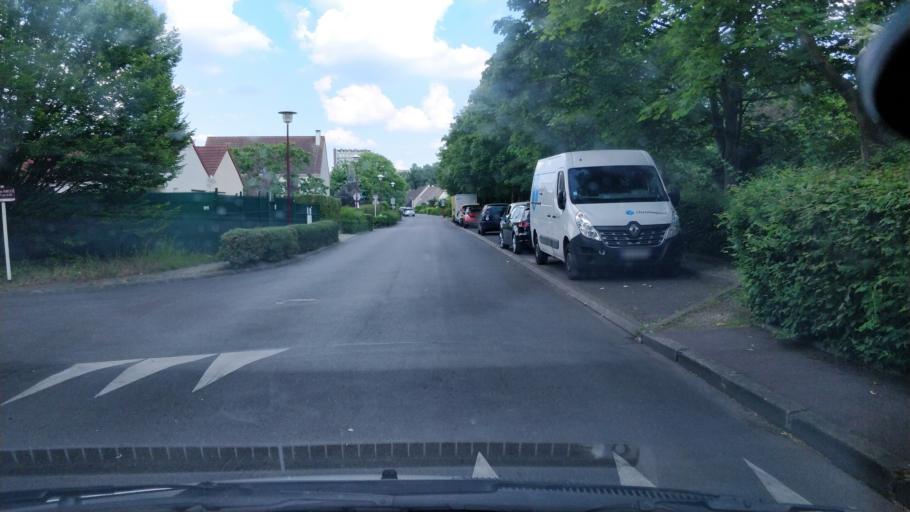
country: FR
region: Ile-de-France
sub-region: Departement de Seine-Saint-Denis
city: Bondy
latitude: 48.8899
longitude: 2.4820
